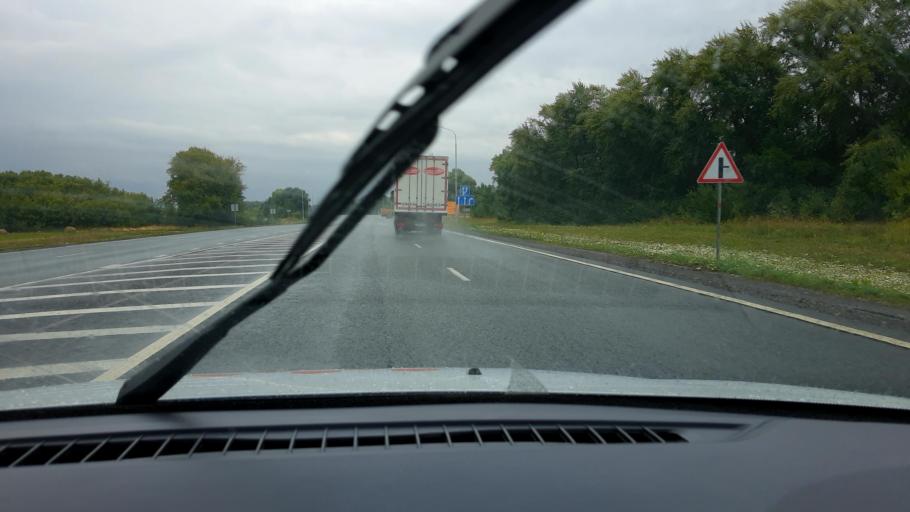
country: RU
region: Chuvashia
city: Yantikovo
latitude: 55.7889
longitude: 47.7281
